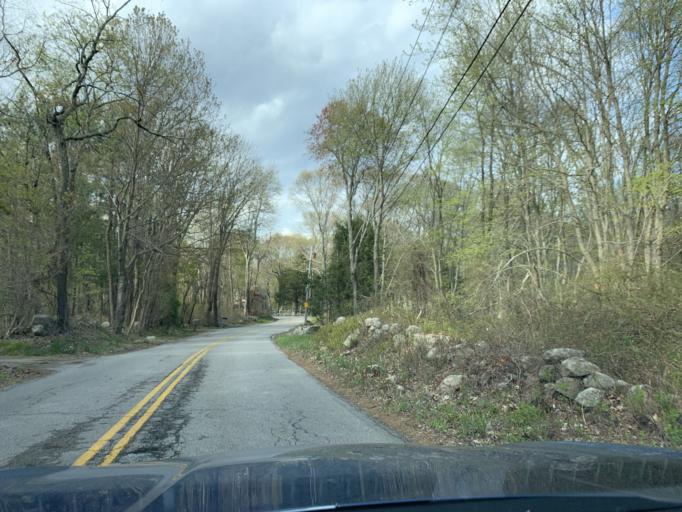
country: US
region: Rhode Island
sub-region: Washington County
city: Exeter
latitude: 41.6017
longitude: -71.5211
